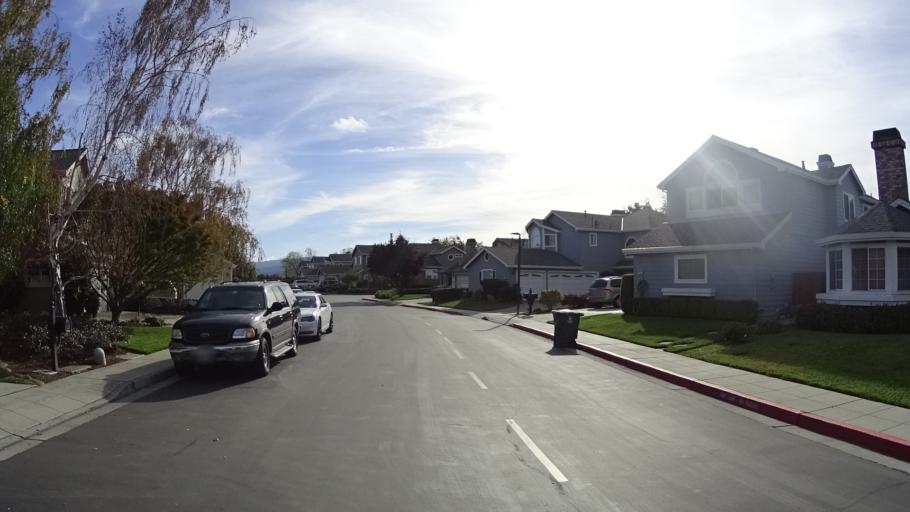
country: US
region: California
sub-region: San Mateo County
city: Redwood Shores
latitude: 37.5429
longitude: -122.2582
